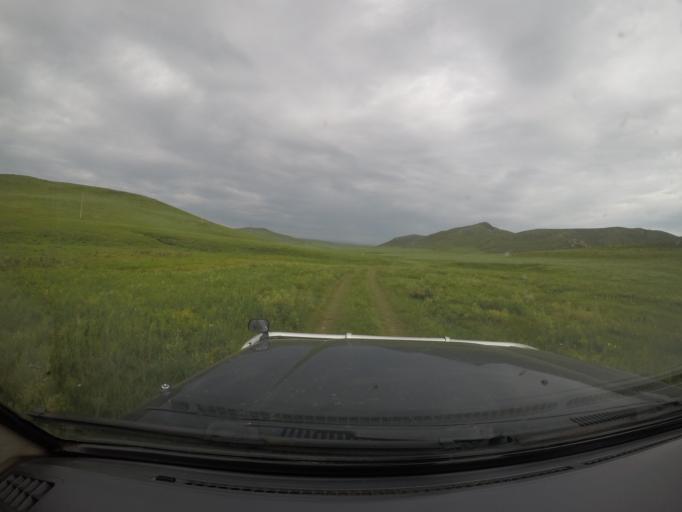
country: MN
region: Suhbaatar
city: Hanhohiy
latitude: 47.6445
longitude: 112.0918
